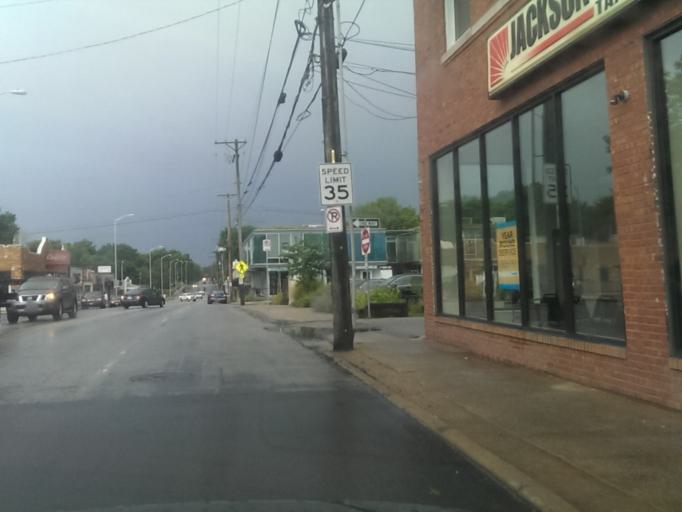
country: US
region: Kansas
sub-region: Johnson County
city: Mission Hills
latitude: 38.9924
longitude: -94.5945
